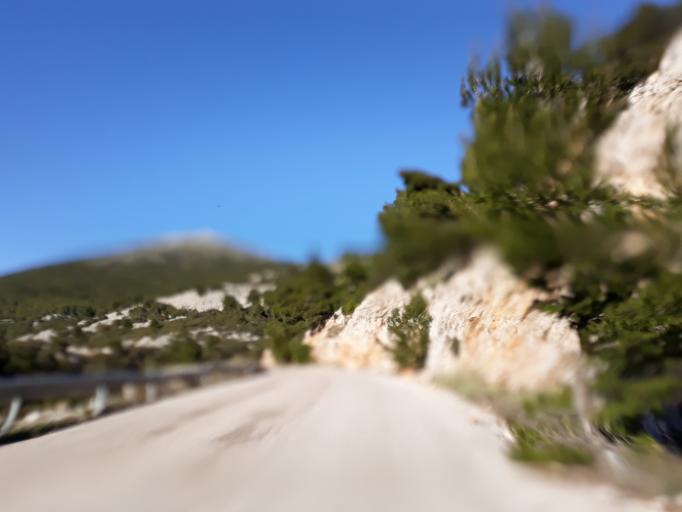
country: GR
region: Attica
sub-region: Nomarchia Dytikis Attikis
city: Fyli
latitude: 38.1384
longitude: 23.6481
